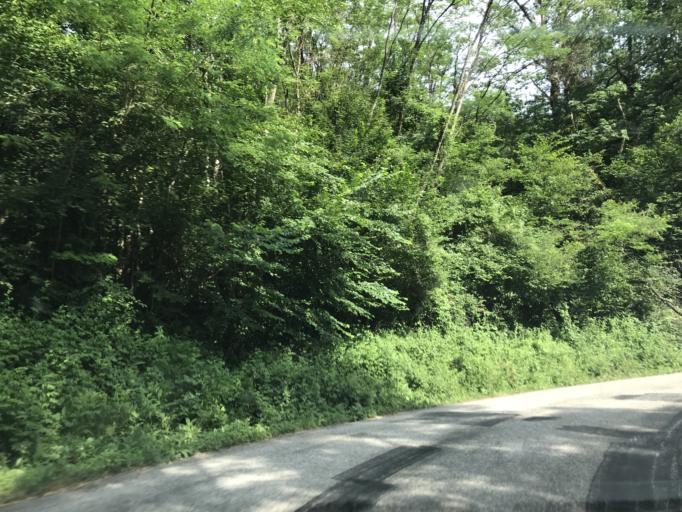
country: FR
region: Rhone-Alpes
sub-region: Departement de la Savoie
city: La Rochette
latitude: 45.4302
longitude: 6.0961
